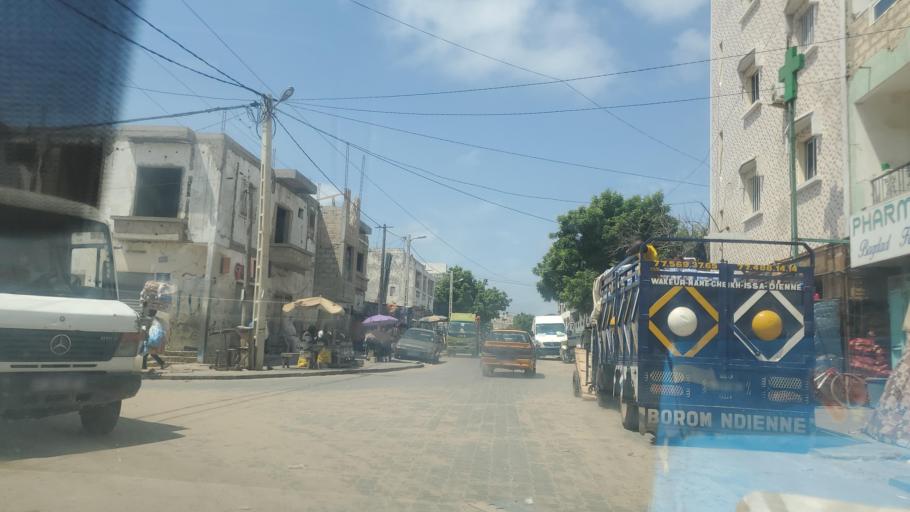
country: SN
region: Dakar
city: Grand Dakar
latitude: 14.7294
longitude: -17.4520
